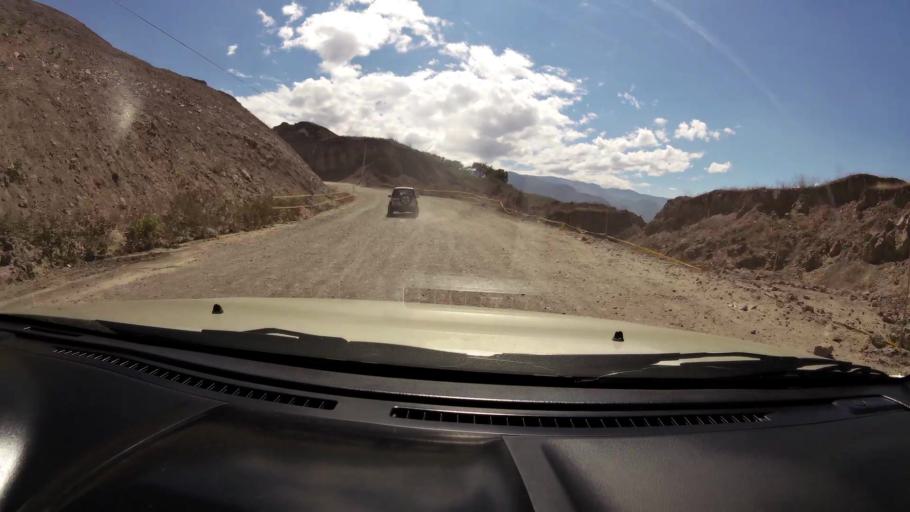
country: EC
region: El Oro
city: Zaruma
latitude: -3.3252
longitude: -79.3544
